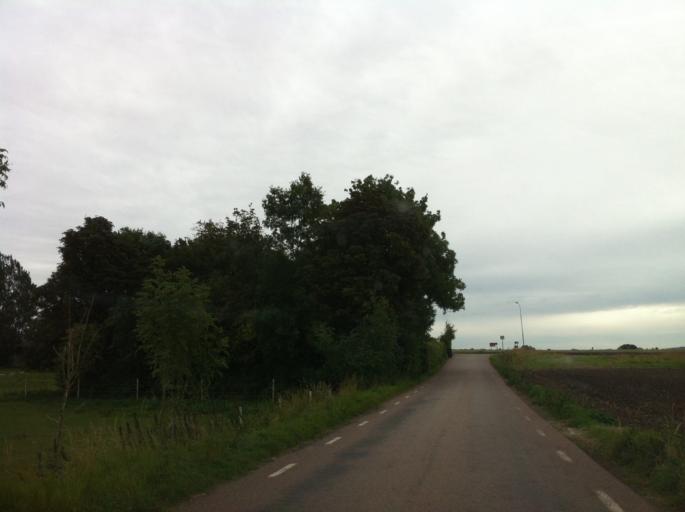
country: SE
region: Skane
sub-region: Svalovs Kommun
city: Teckomatorp
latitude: 55.8999
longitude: 13.0182
